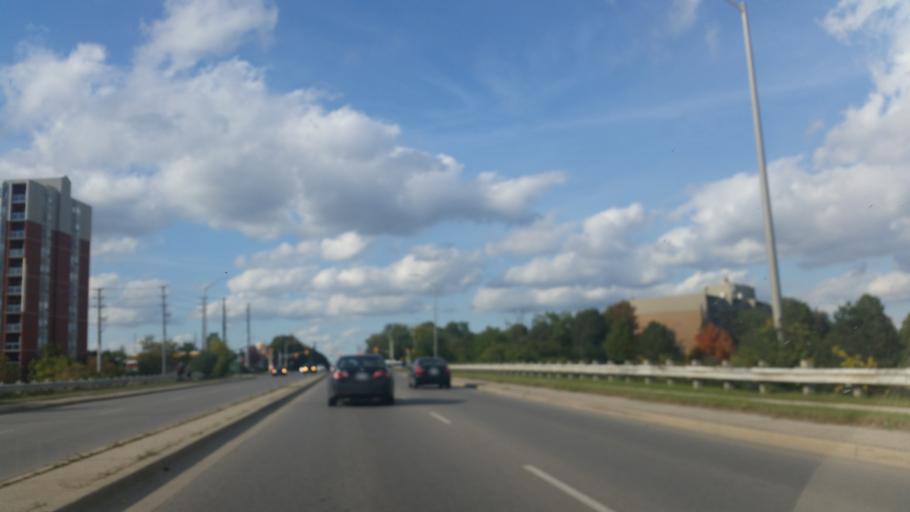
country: CA
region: Ontario
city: London
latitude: 42.9929
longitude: -81.2973
